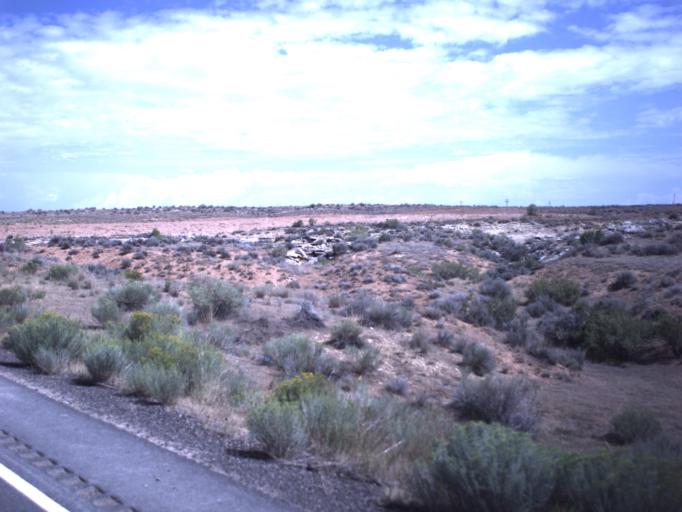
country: US
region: Utah
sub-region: Uintah County
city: Naples
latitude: 40.1963
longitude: -109.3343
